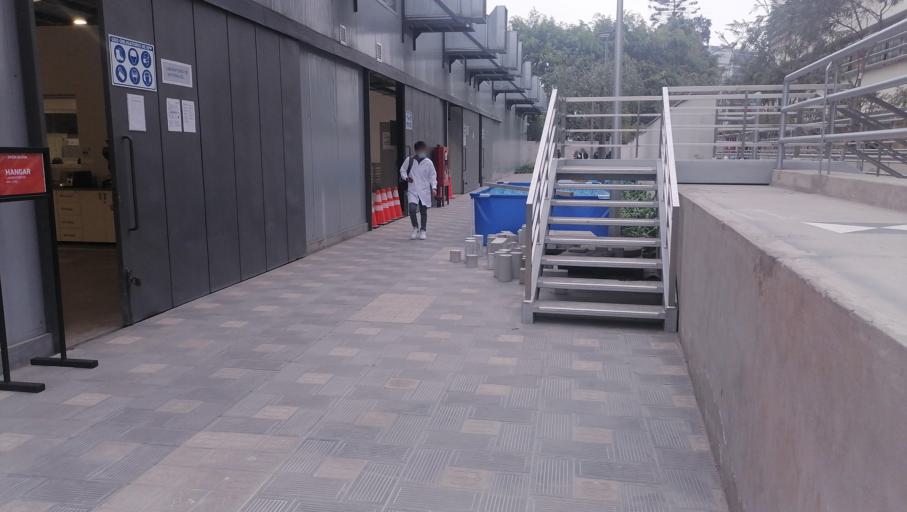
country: PE
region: Lima
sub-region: Lima
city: La Molina
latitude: -12.0854
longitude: -76.9698
